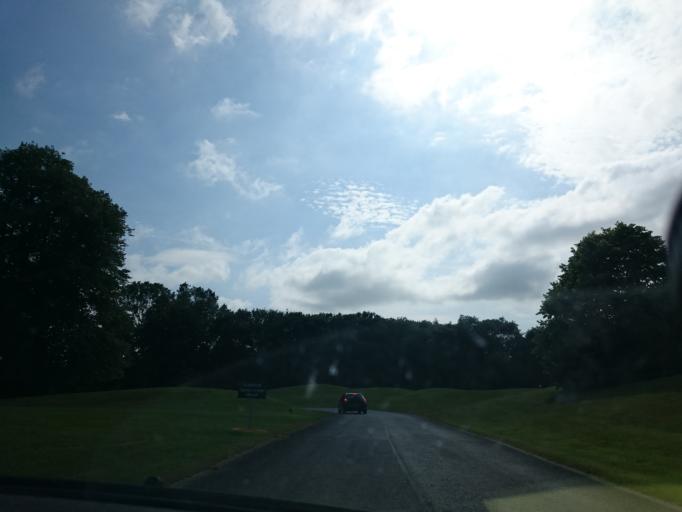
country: IE
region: Leinster
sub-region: Kilkenny
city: Thomastown
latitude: 52.5213
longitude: -7.1909
